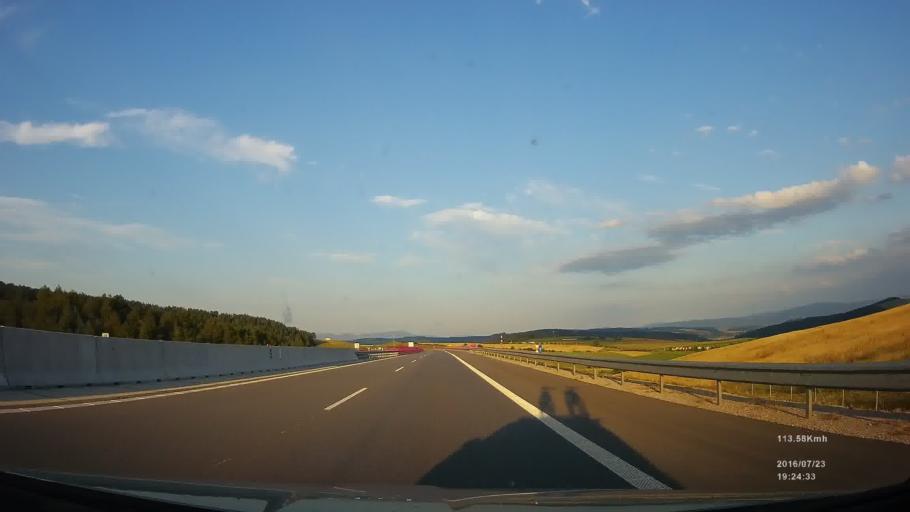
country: SK
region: Kosicky
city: Spisska Nova Ves
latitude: 49.0014
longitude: 20.5103
